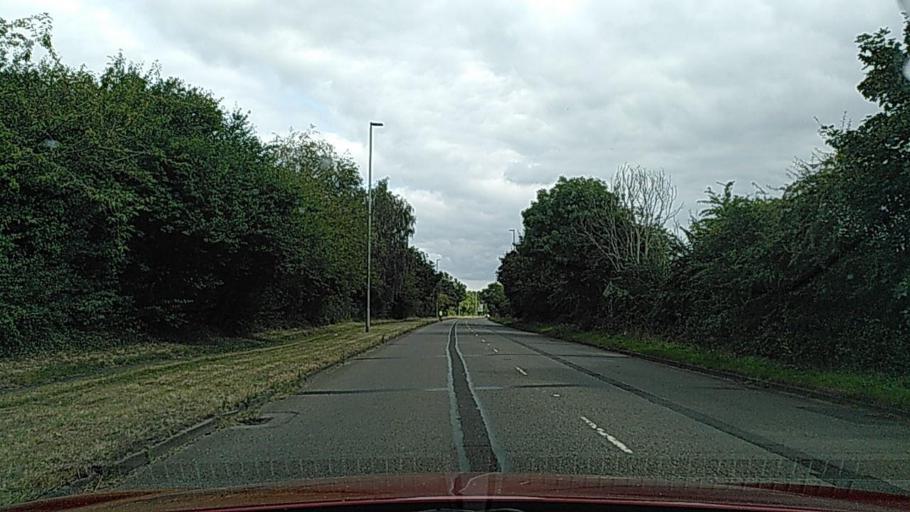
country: GB
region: England
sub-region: Wokingham
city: Wargrave
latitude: 51.4924
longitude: -0.8577
